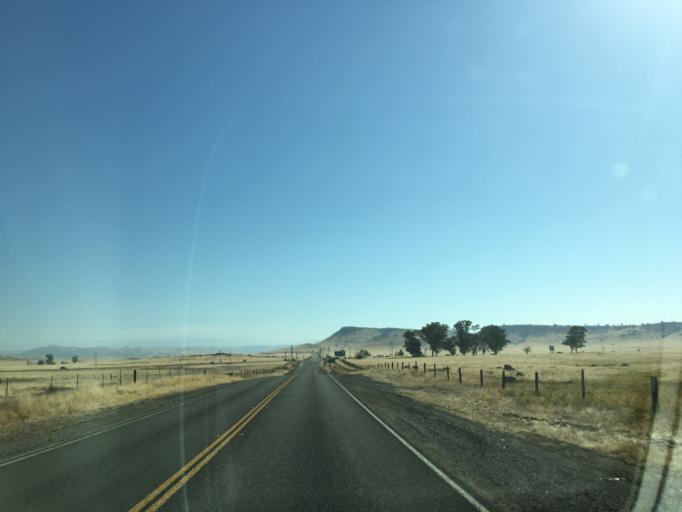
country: US
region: California
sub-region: Madera County
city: Bonadelle Ranchos-Madera Ranchos
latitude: 37.0105
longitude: -119.7999
